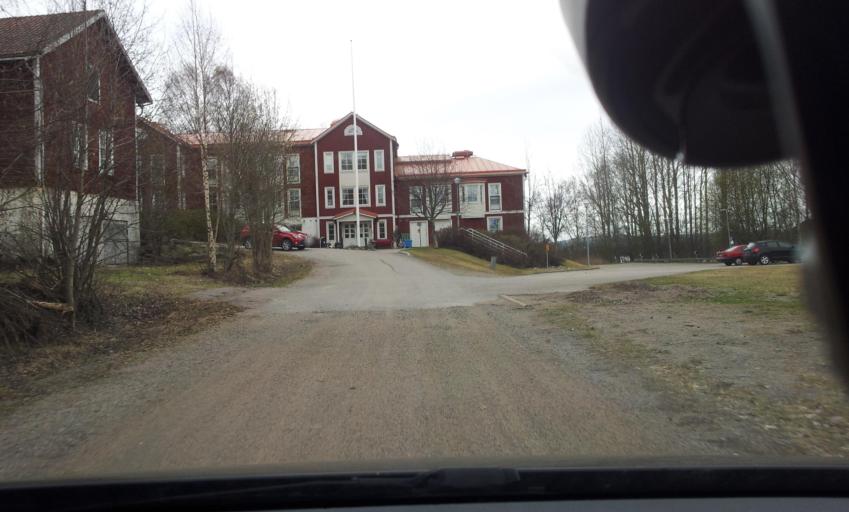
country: SE
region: Gaevleborg
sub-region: Ljusdals Kommun
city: Farila
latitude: 61.8021
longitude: 15.8443
